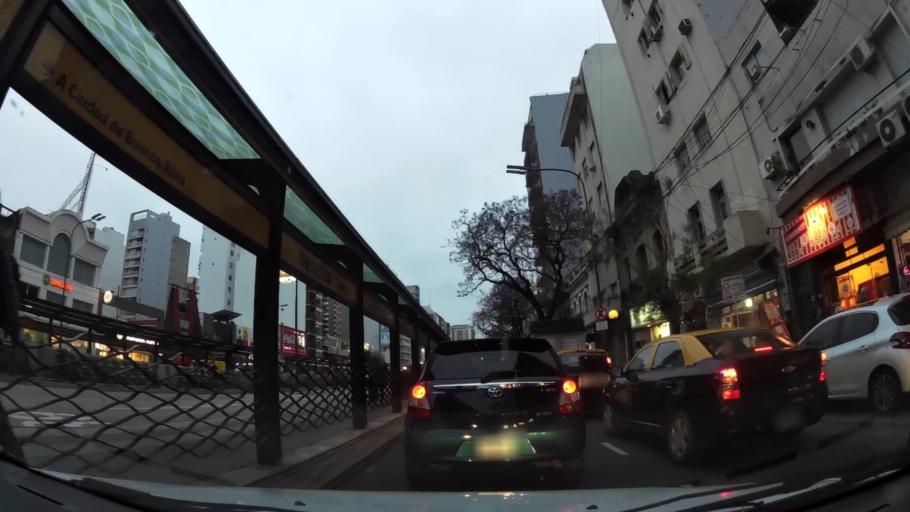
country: AR
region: Buenos Aires F.D.
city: Colegiales
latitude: -34.5548
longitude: -58.4635
